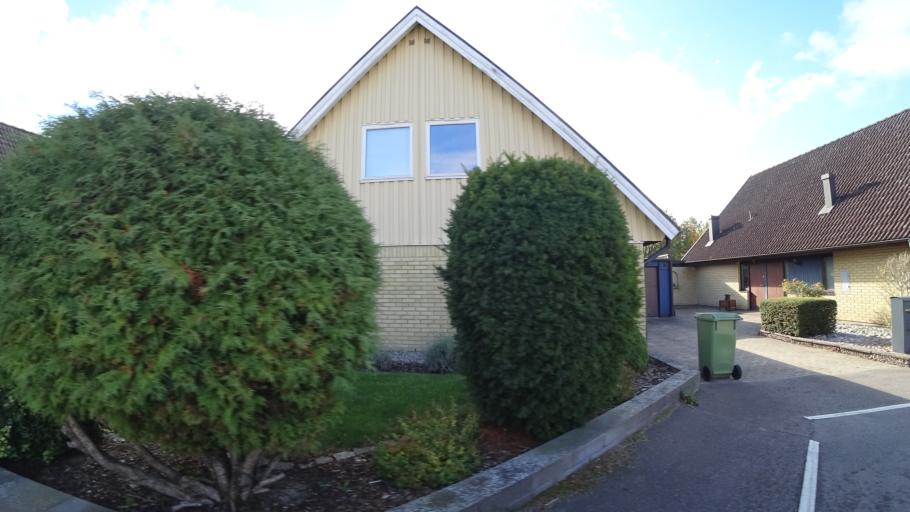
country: SE
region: Skane
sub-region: Staffanstorps Kommun
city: Staffanstorp
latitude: 55.6324
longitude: 13.1906
